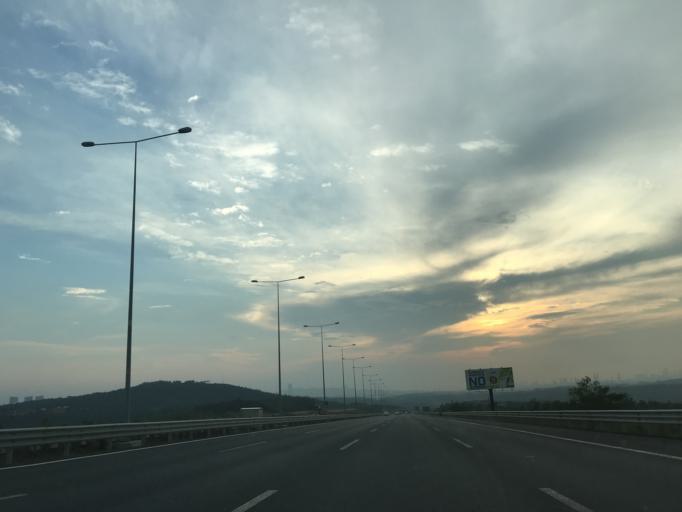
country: TR
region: Istanbul
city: Umraniye
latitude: 41.0508
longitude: 29.1600
